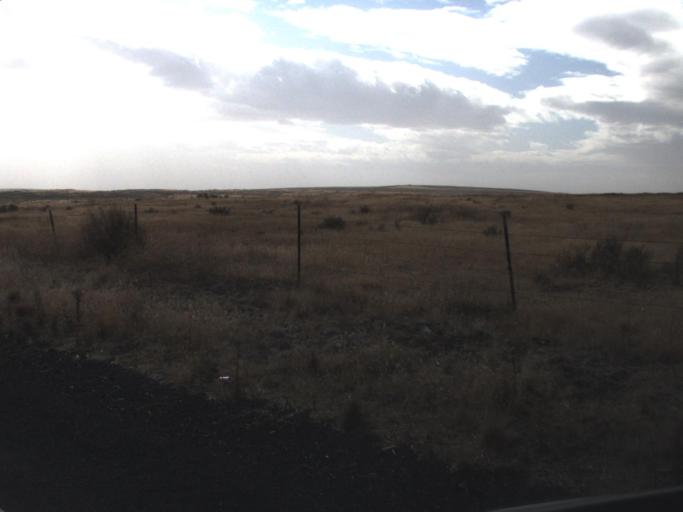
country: US
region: Washington
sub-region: Okanogan County
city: Coulee Dam
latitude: 47.5489
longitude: -118.7855
